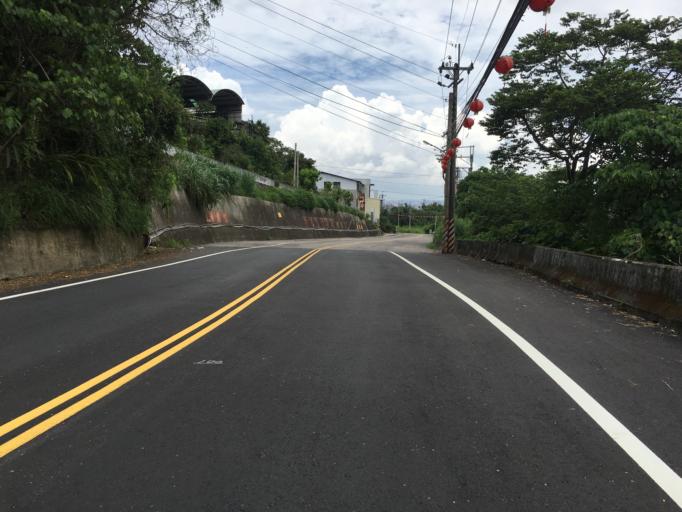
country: TW
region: Taiwan
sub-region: Taichung City
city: Taichung
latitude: 24.0742
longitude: 120.7270
